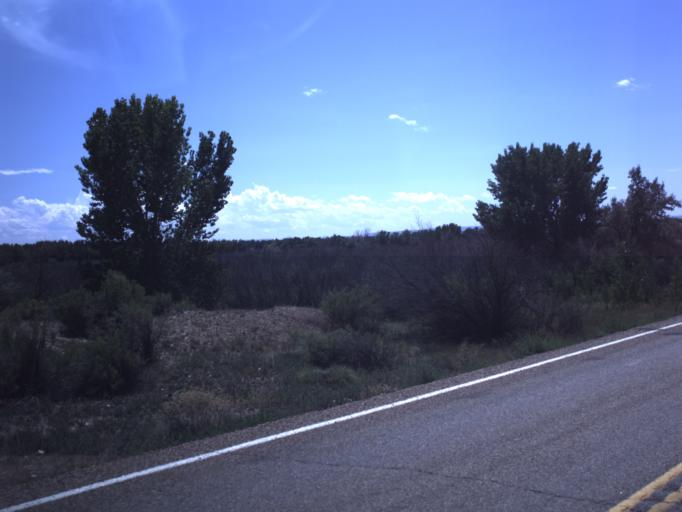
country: US
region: Utah
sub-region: Uintah County
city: Naples
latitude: 40.1024
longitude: -109.6734
